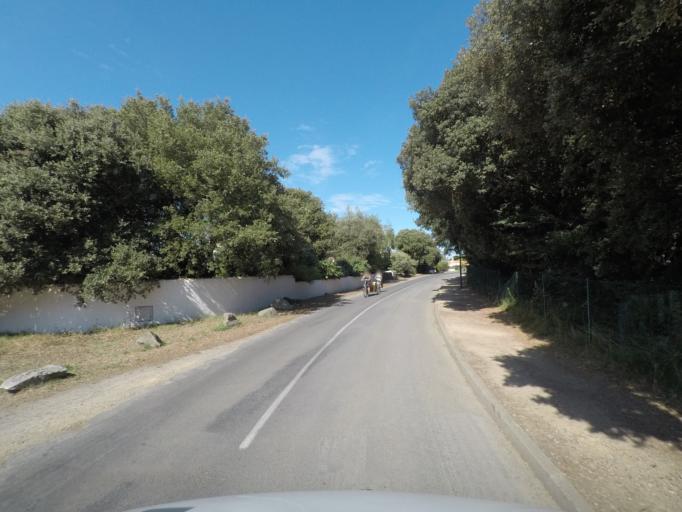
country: FR
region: Pays de la Loire
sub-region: Departement de la Vendee
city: La Gueriniere
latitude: 46.9977
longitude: -2.2245
